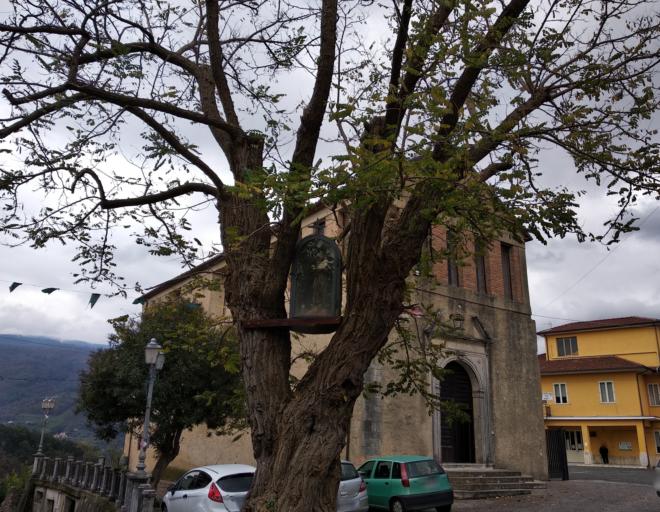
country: IT
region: Calabria
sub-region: Provincia di Catanzaro
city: Martirano
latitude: 39.0787
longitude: 16.2484
